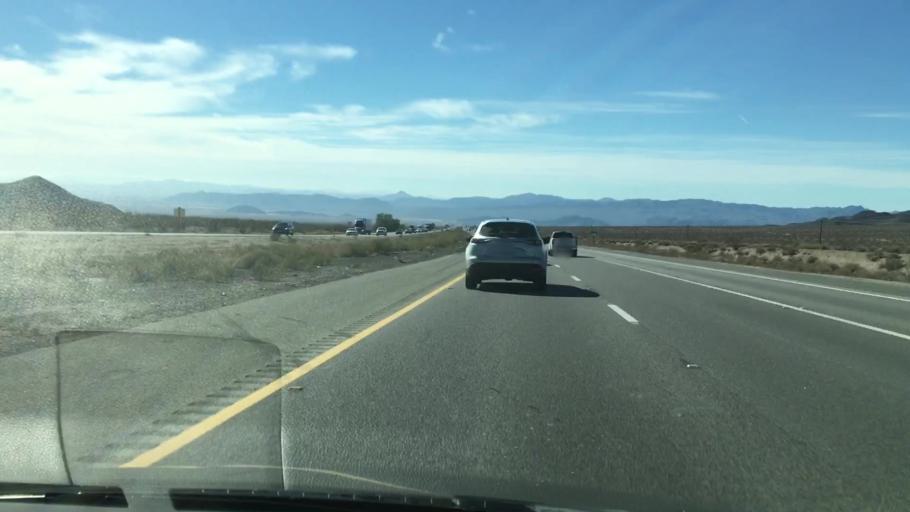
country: US
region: Nevada
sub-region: Clark County
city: Sandy Valley
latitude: 35.3666
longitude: -115.9149
